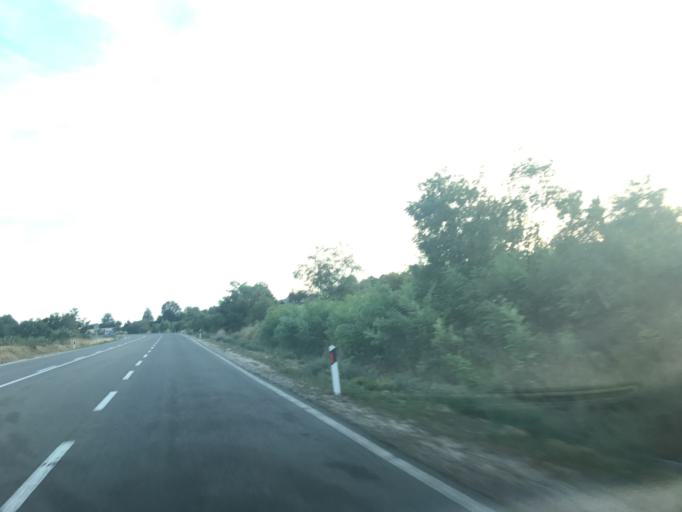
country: RS
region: Central Serbia
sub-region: Zajecarski Okrug
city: Boljevac
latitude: 43.8722
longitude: 21.9647
